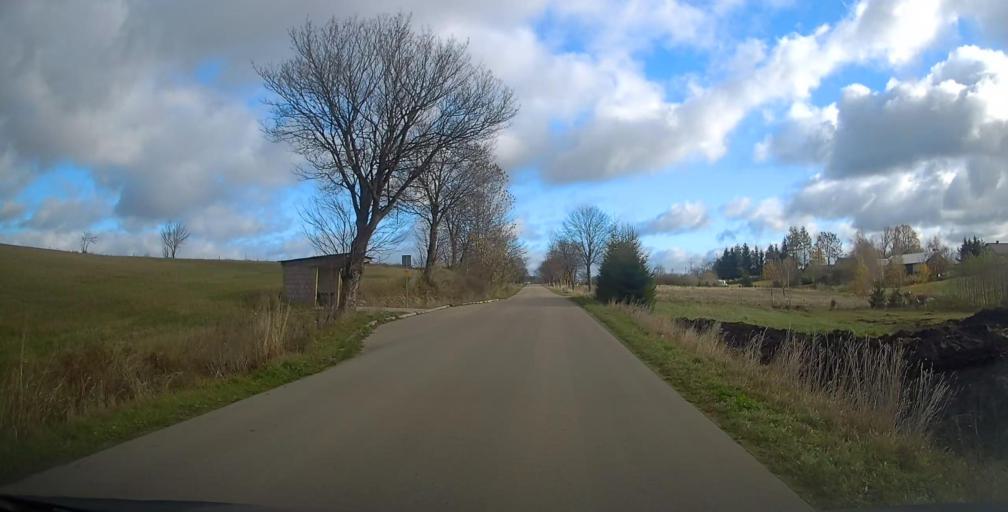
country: PL
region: Podlasie
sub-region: Suwalki
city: Suwalki
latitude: 54.3167
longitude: 22.8691
